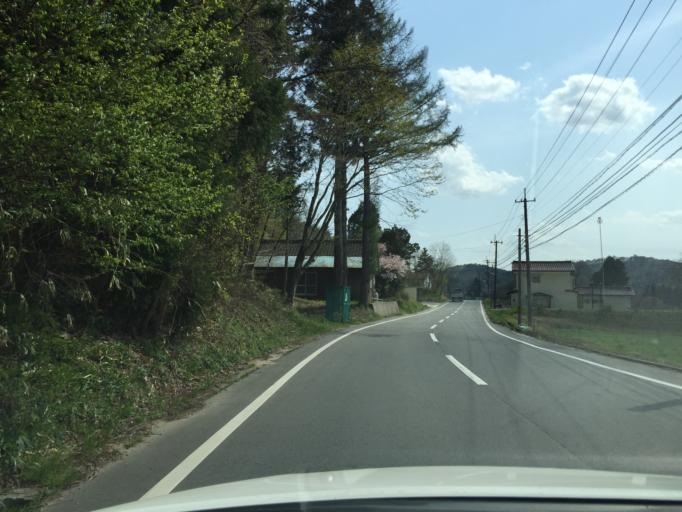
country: JP
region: Fukushima
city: Namie
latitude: 37.3548
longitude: 140.8062
